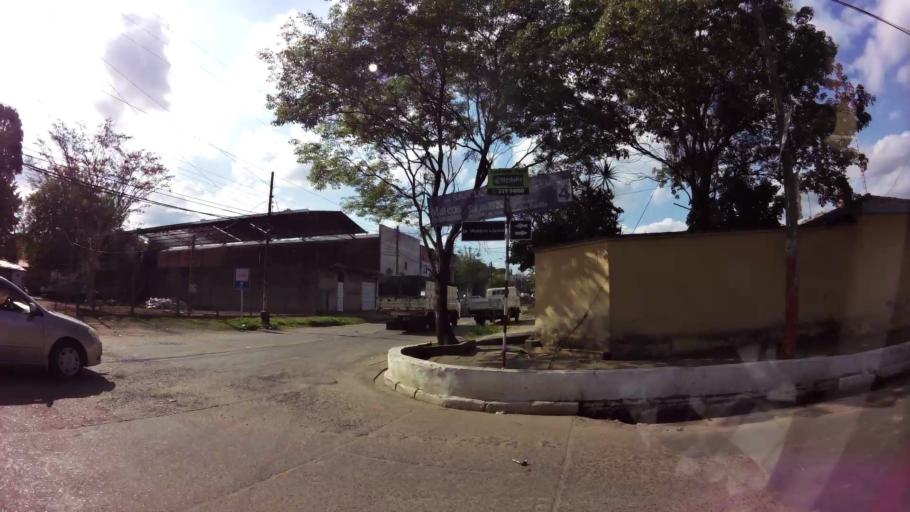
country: PY
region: Central
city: Fernando de la Mora
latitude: -25.3145
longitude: -57.5368
